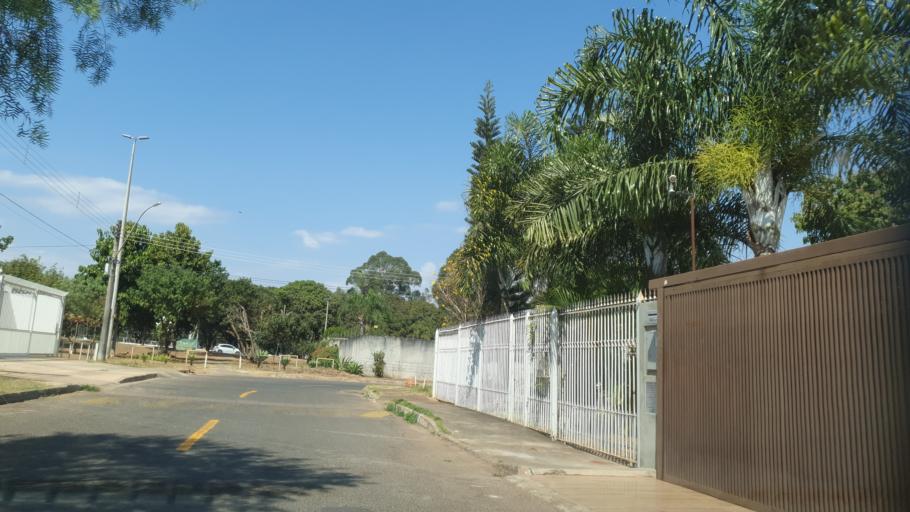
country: BR
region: Federal District
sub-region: Brasilia
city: Brasilia
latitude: -15.7887
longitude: -47.9330
